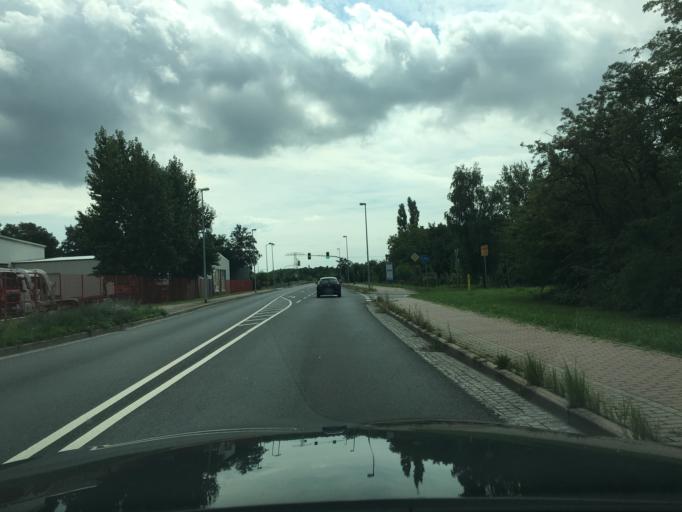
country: DE
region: Saxony-Anhalt
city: Sandersdorf
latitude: 51.6409
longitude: 12.2792
